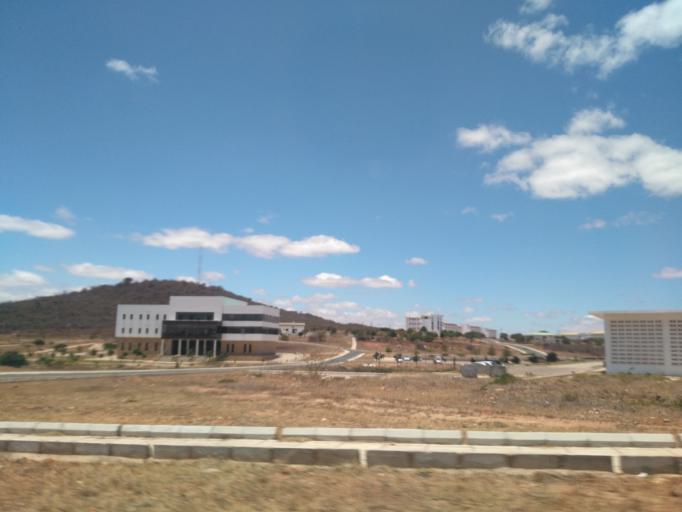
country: TZ
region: Dodoma
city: Kisasa
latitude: -6.2157
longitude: 35.8079
